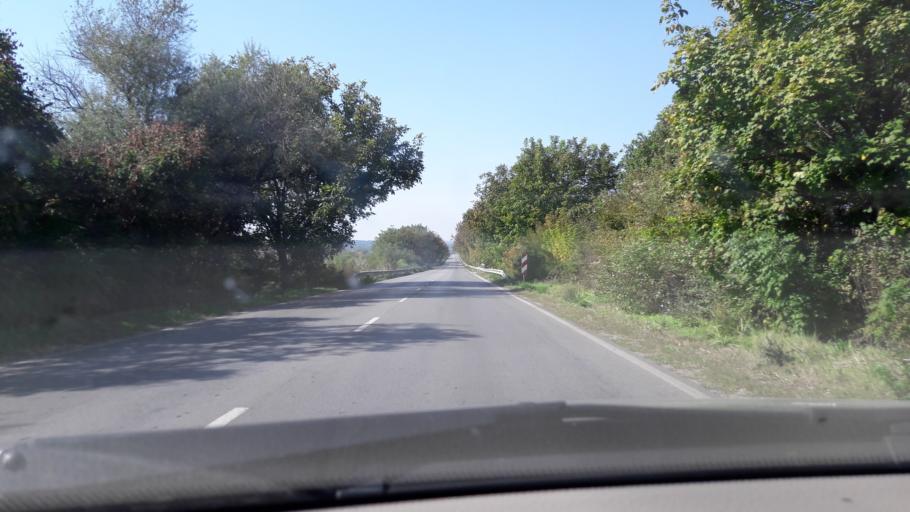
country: BG
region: Razgrad
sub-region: Obshtina Razgrad
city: Razgrad
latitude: 43.5454
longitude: 26.4946
